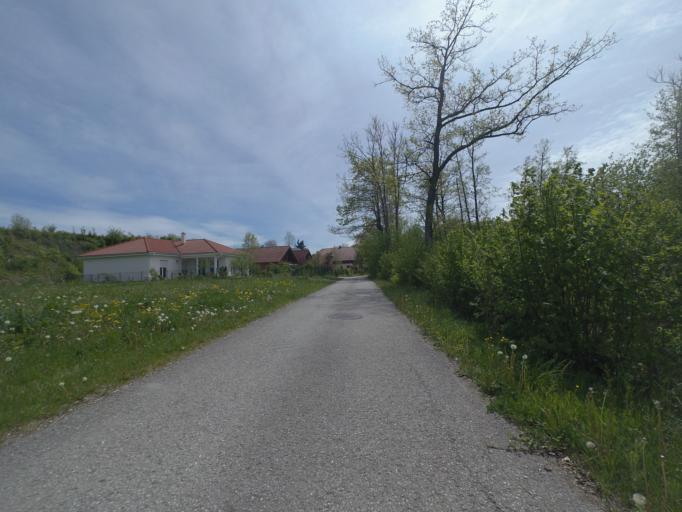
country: AT
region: Salzburg
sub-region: Politischer Bezirk Salzburg-Umgebung
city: Mattsee
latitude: 48.0001
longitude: 13.1191
